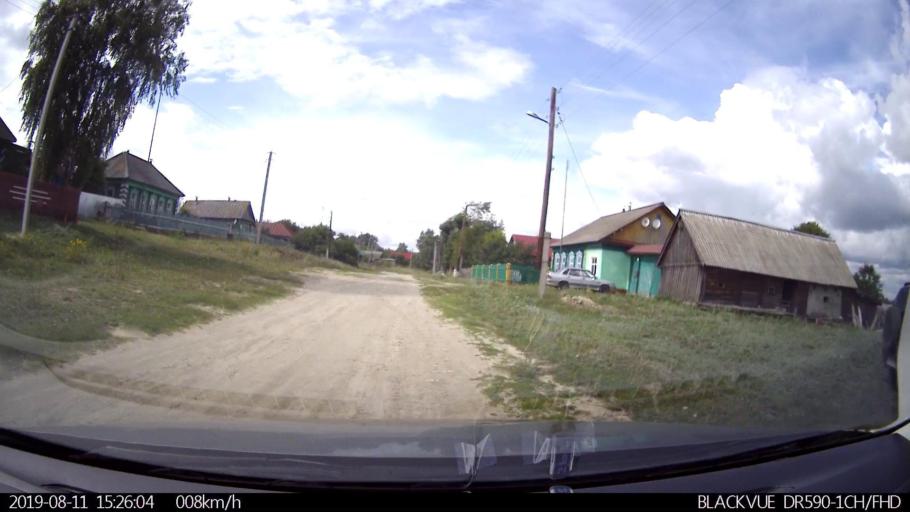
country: RU
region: Ulyanovsk
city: Ignatovka
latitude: 53.8497
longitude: 47.5765
